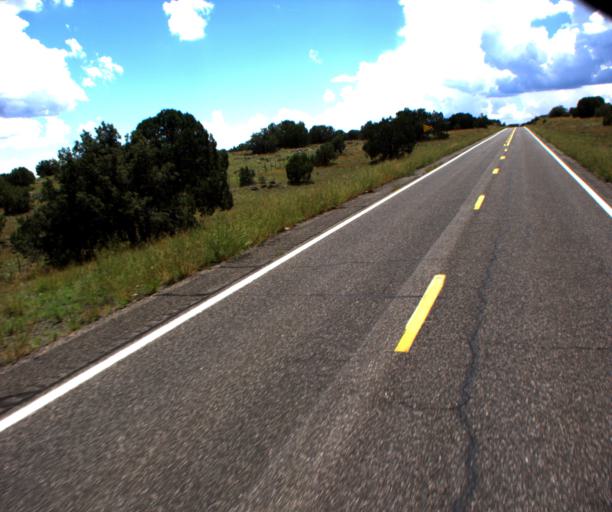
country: US
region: Arizona
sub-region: Gila County
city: Pine
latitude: 34.4946
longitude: -111.5895
